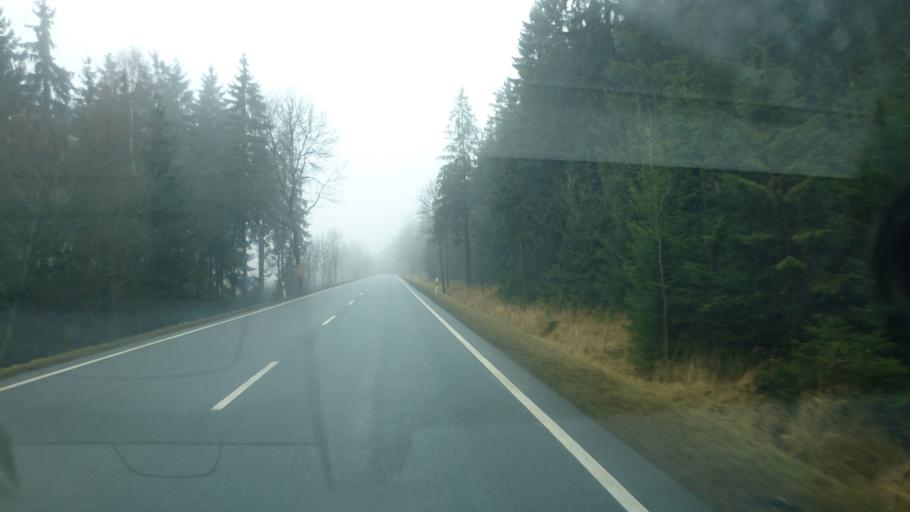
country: DE
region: Thuringia
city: Tanna
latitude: 50.4780
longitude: 11.8383
